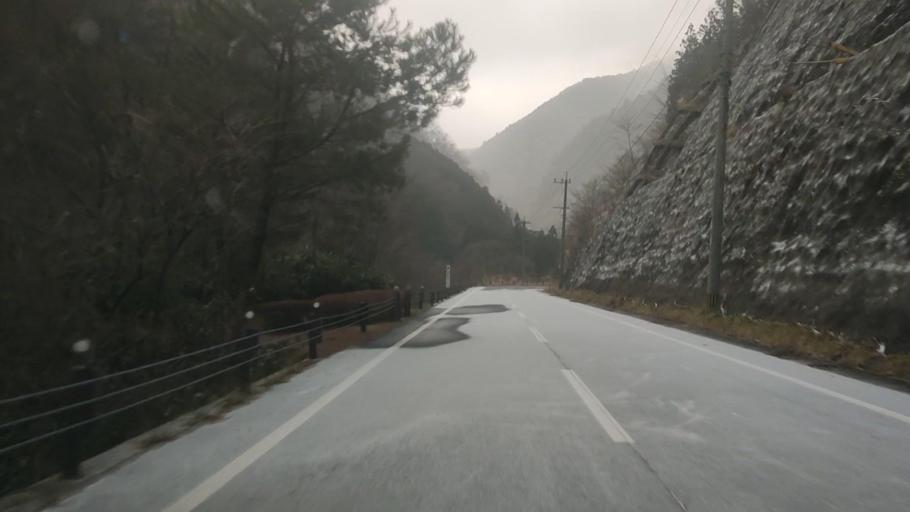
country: JP
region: Kumamoto
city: Matsubase
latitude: 32.5589
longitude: 130.9188
